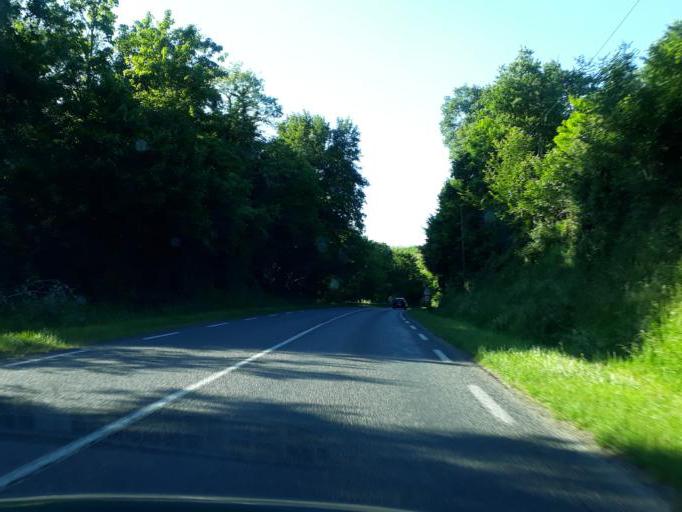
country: FR
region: Bourgogne
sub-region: Departement de la Nievre
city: Neuvy-sur-Loire
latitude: 47.4844
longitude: 2.9237
